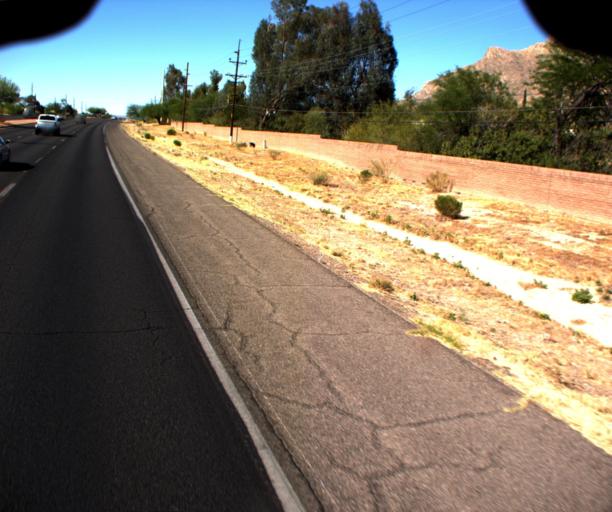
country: US
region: Arizona
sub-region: Pima County
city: Oro Valley
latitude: 32.3563
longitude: -110.9736
